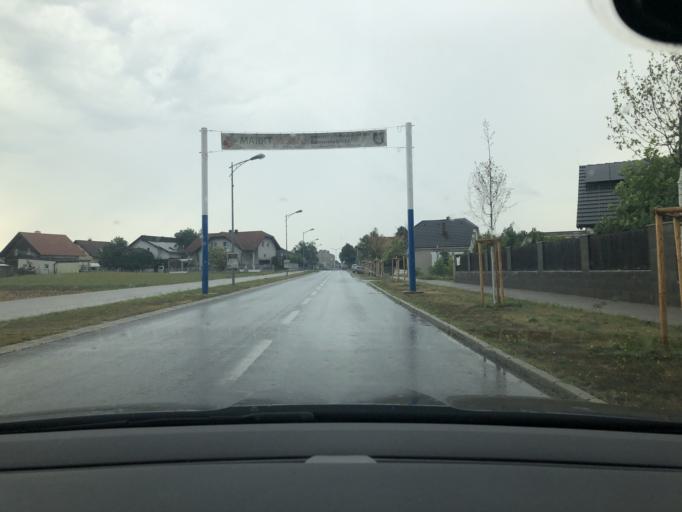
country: AT
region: Lower Austria
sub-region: Politischer Bezirk Ganserndorf
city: Ganserndorf
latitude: 48.3386
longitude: 16.7365
